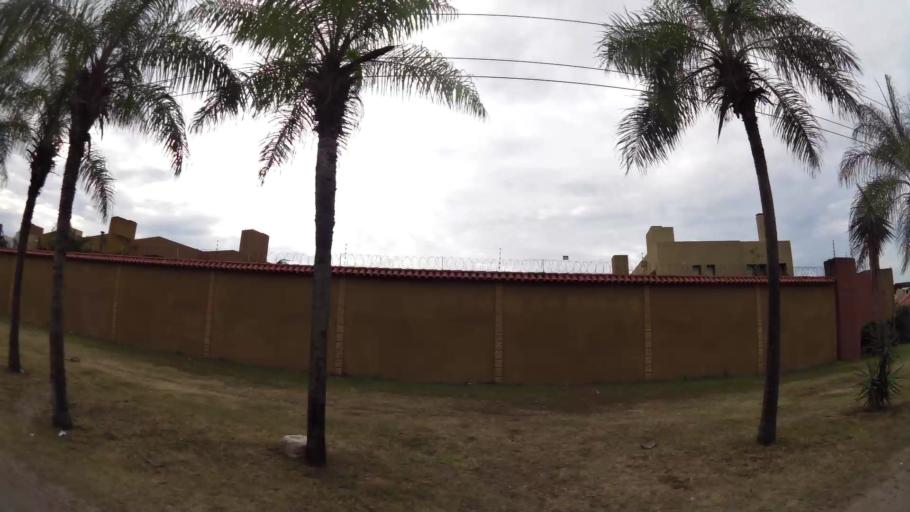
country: BO
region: Santa Cruz
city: Santa Cruz de la Sierra
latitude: -17.7393
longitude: -63.1624
